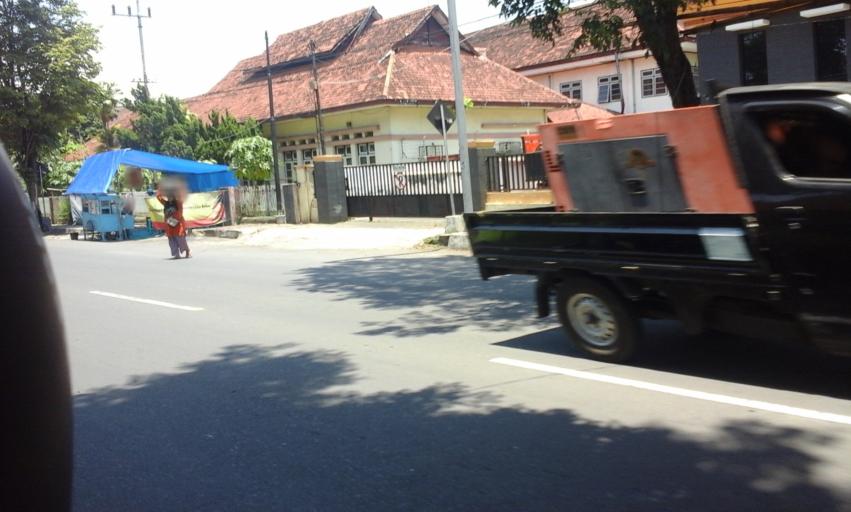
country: ID
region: East Java
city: Sumberdangdang
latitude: -8.1793
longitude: 113.7083
